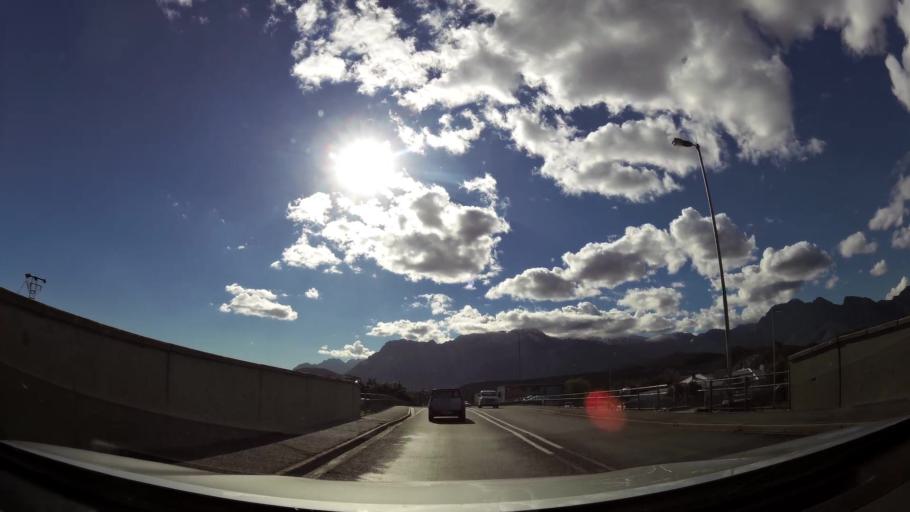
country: ZA
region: Western Cape
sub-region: Cape Winelands District Municipality
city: Worcester
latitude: -33.6400
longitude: 19.4315
